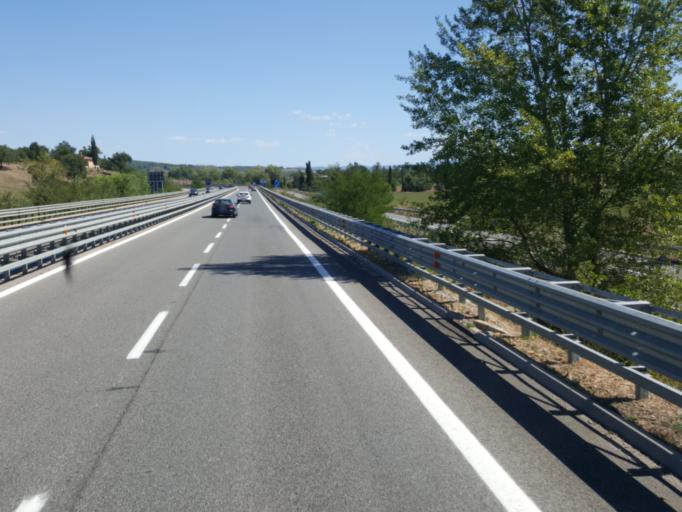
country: IT
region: Tuscany
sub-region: Provincia di Grosseto
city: Campagnatico
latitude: 42.9207
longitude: 11.2608
